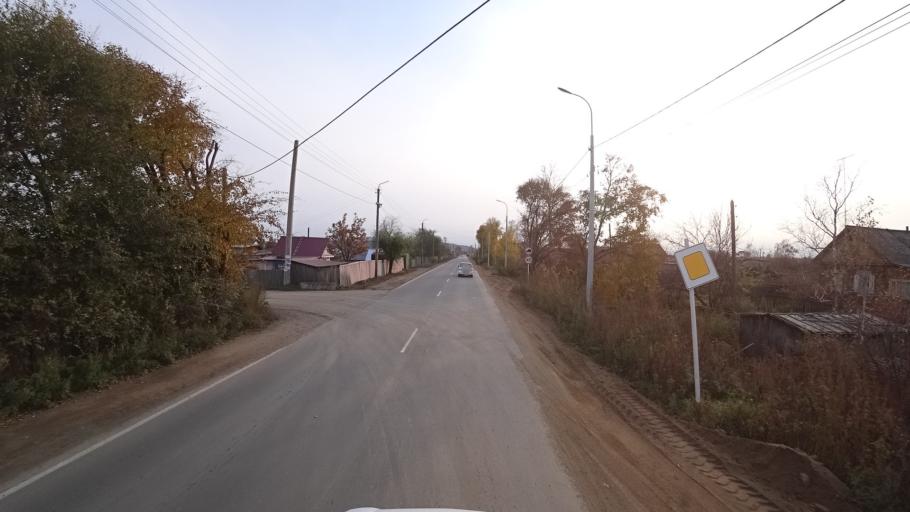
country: RU
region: Khabarovsk Krai
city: Amursk
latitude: 50.0882
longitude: 136.5008
